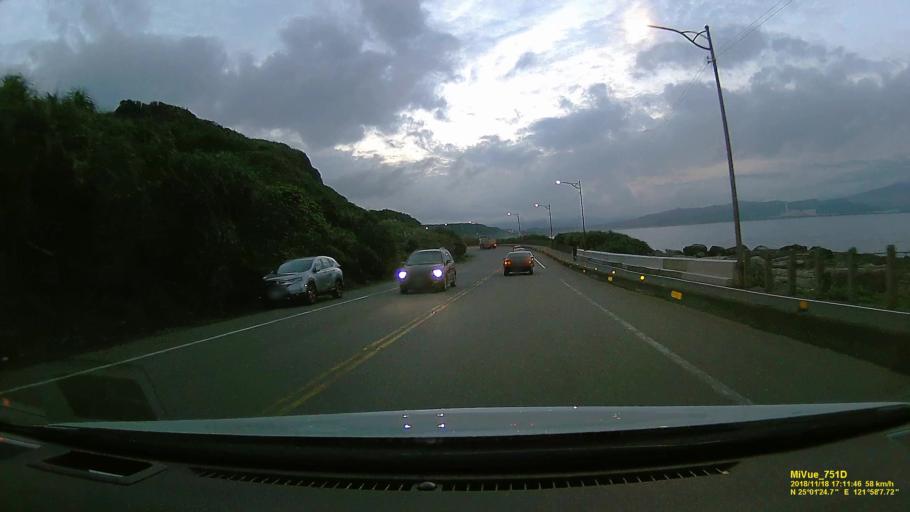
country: TW
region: Taiwan
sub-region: Keelung
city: Keelung
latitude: 25.0235
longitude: 121.9686
